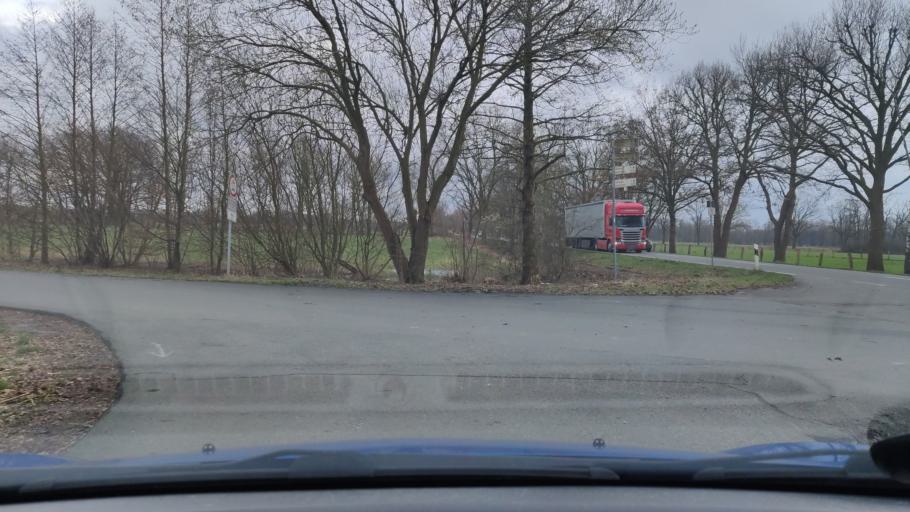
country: DE
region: Lower Saxony
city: Garbsen-Mitte
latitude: 52.4665
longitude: 9.6439
